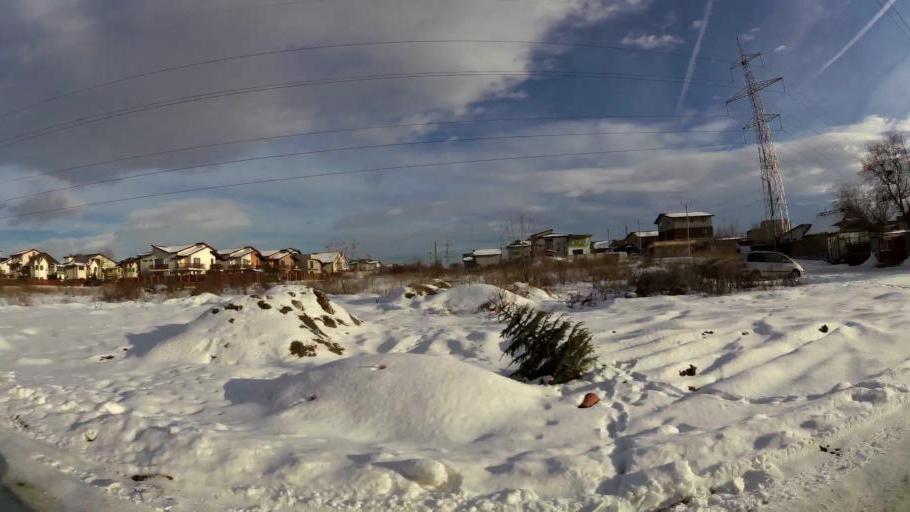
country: RO
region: Ilfov
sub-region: Comuna Fundeni-Dobroesti
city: Fundeni
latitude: 44.4636
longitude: 26.1743
